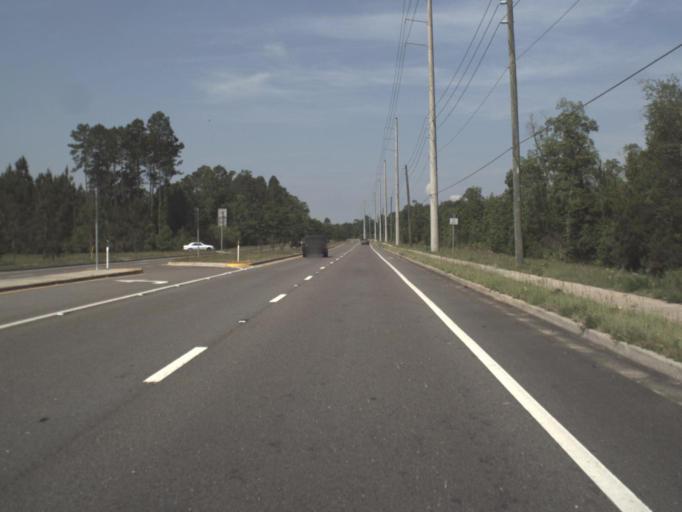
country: US
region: Florida
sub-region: Saint Johns County
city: Saint Augustine Shores
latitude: 29.8081
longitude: -81.4022
